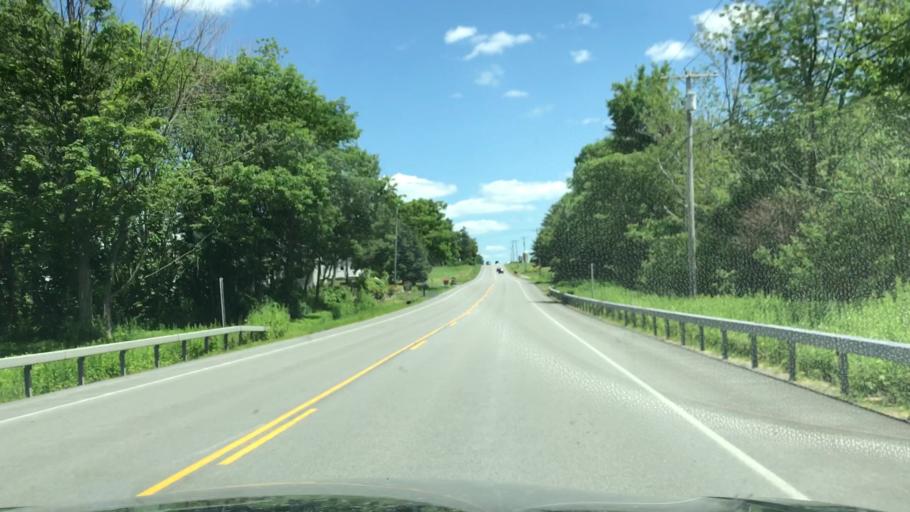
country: US
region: New York
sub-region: Erie County
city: Alden
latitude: 42.7698
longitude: -78.4293
